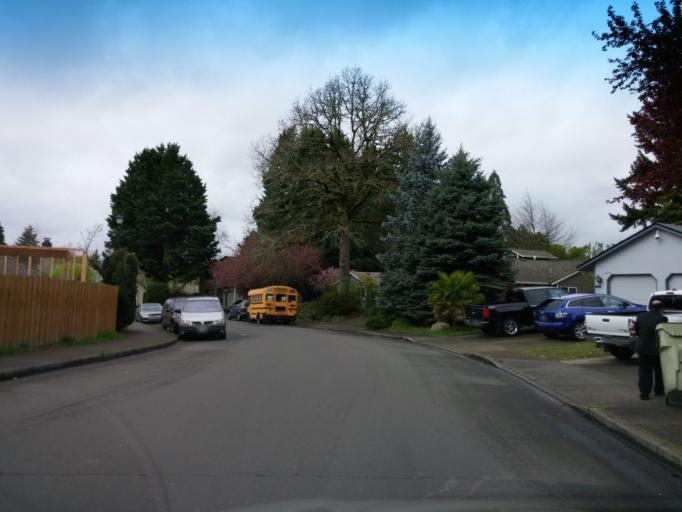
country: US
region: Oregon
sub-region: Washington County
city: Aloha
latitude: 45.5107
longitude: -122.8606
